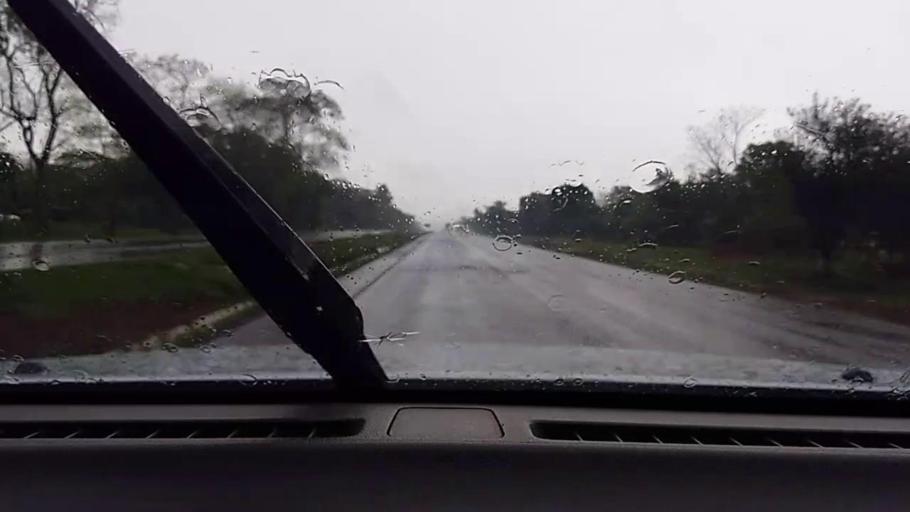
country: PY
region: Caaguazu
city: Repatriacion
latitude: -25.4506
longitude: -55.9001
